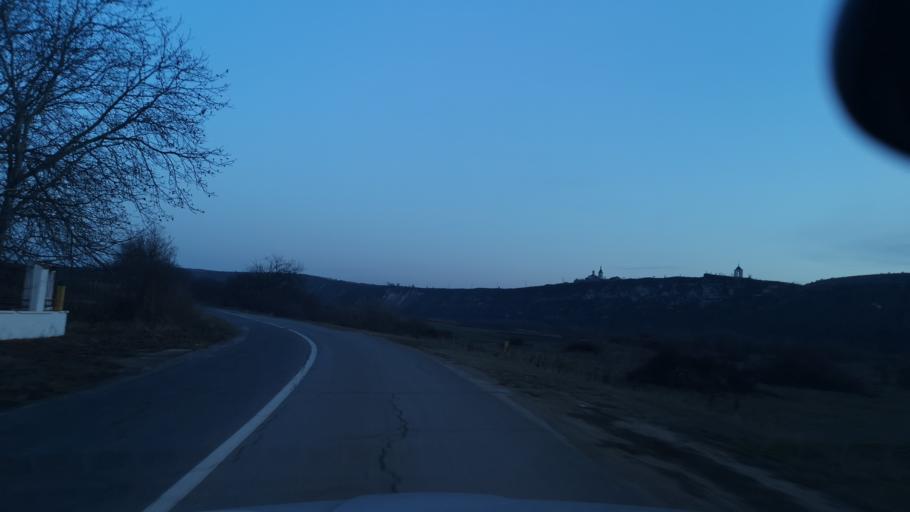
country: MD
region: Telenesti
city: Cocieri
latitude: 47.3070
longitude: 28.9649
